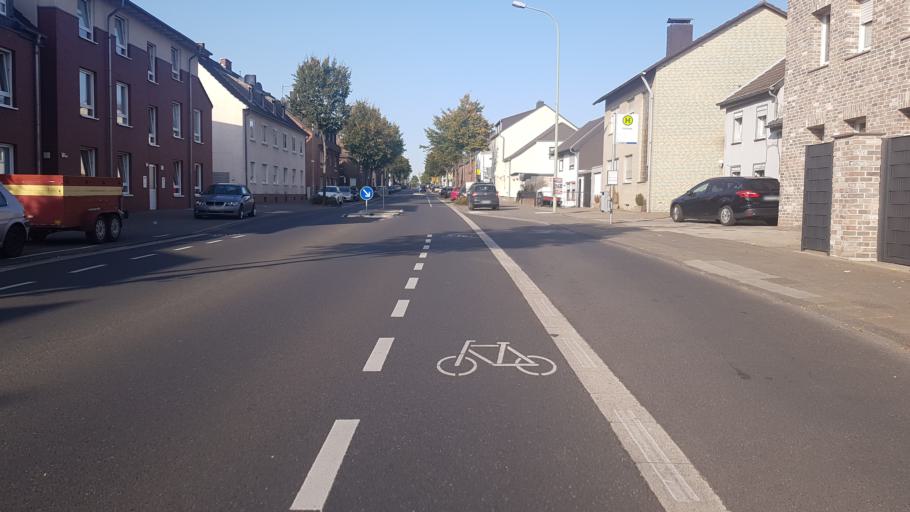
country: DE
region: North Rhine-Westphalia
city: Baesweiler
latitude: 50.9077
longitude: 6.1892
